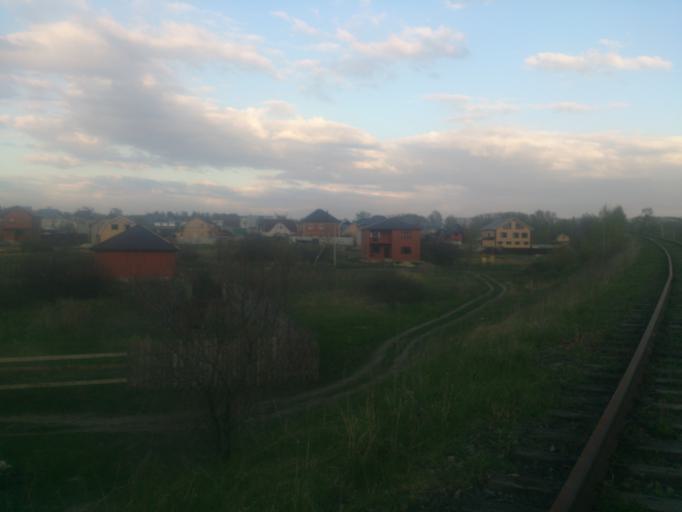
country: RU
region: Ulyanovsk
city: Novoul'yanovsk
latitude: 54.2180
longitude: 48.2868
